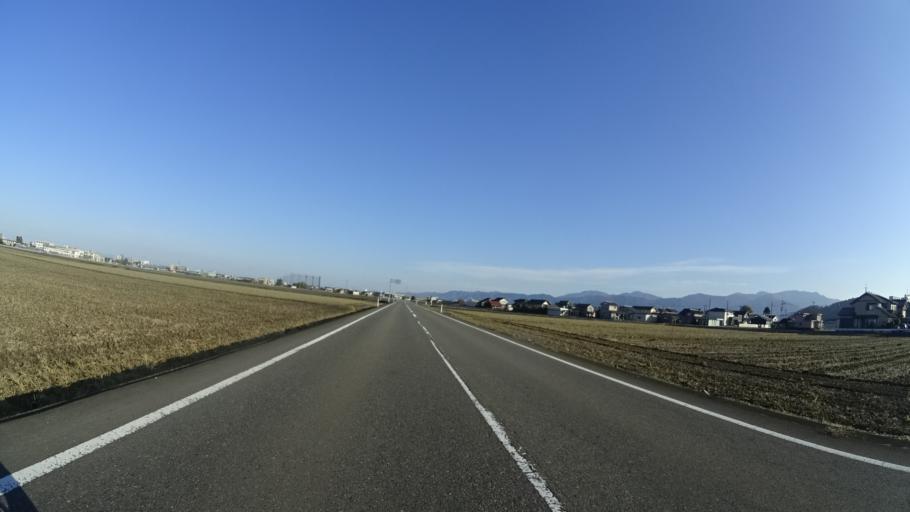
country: JP
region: Fukui
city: Fukui-shi
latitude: 36.0736
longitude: 136.2574
